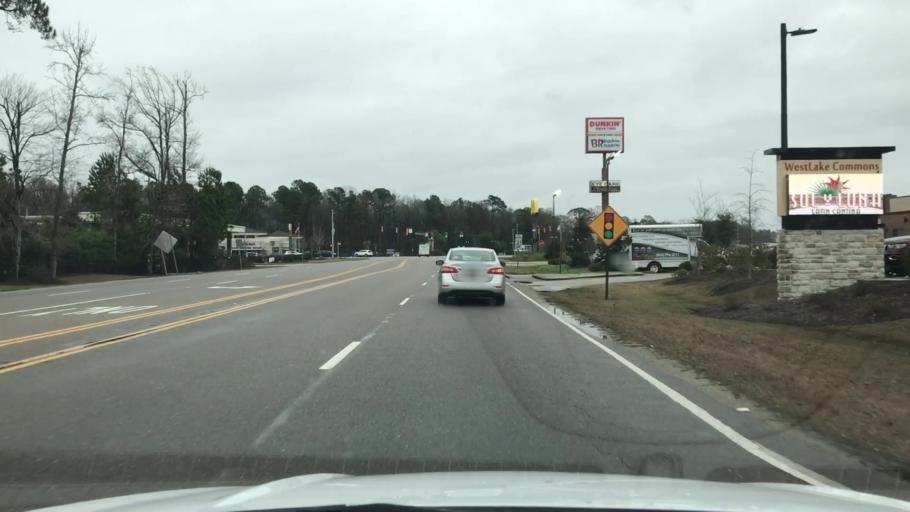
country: US
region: South Carolina
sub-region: Horry County
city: Myrtle Beach
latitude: 33.7595
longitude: -78.8611
